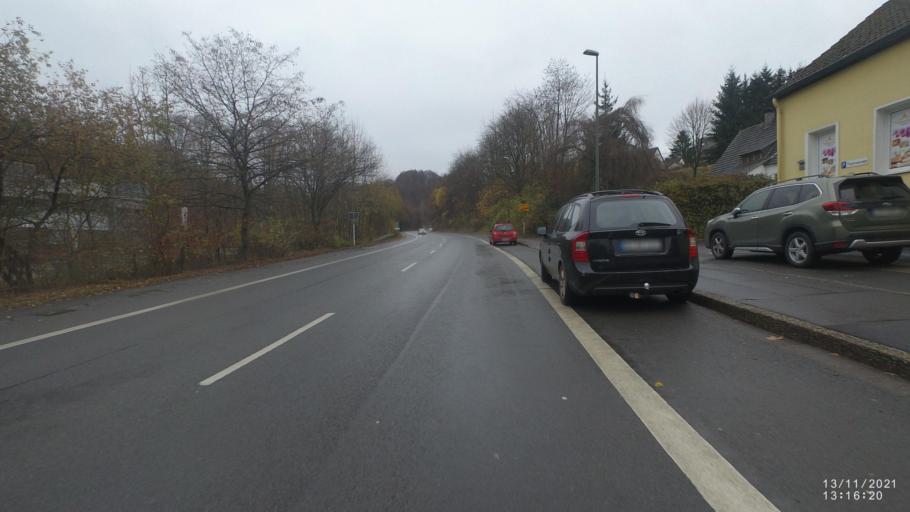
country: DE
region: North Rhine-Westphalia
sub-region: Regierungsbezirk Arnsberg
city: Luedenscheid
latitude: 51.2423
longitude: 7.6248
